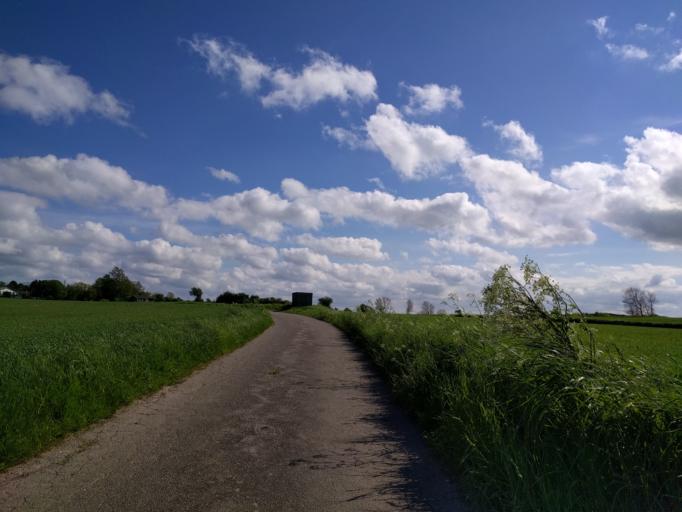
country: DK
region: Zealand
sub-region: Guldborgsund Kommune
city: Stubbekobing
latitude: 54.9355
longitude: 12.0443
